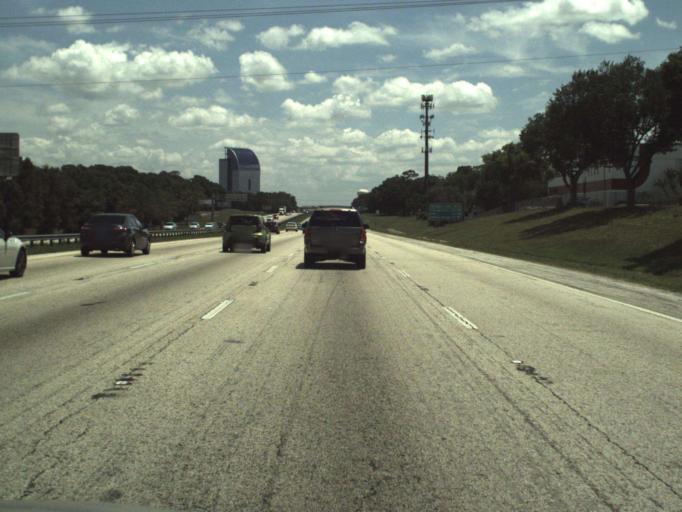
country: US
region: Florida
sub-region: Seminole County
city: Altamonte Springs
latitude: 28.6839
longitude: -81.3889
